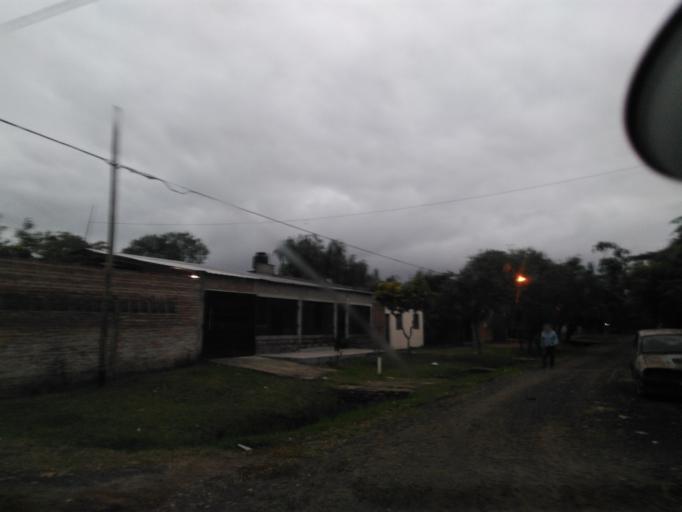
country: AR
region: Chaco
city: Resistencia
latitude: -27.4807
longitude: -58.9947
